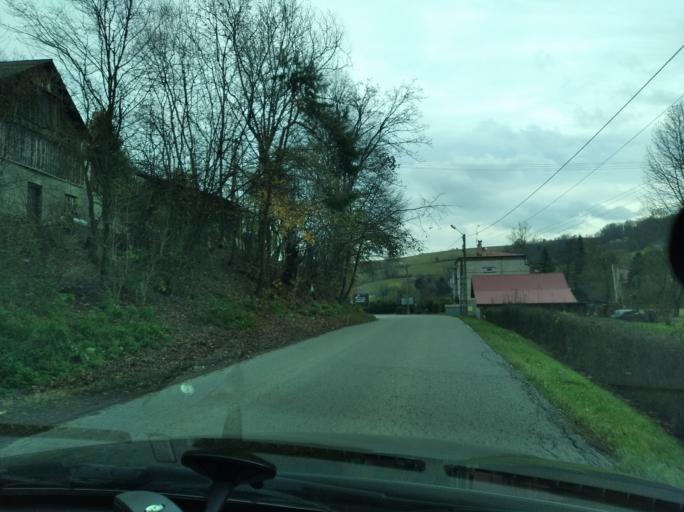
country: PL
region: Subcarpathian Voivodeship
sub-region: Powiat ropczycko-sedziszowski
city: Iwierzyce
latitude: 49.9488
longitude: 21.7302
